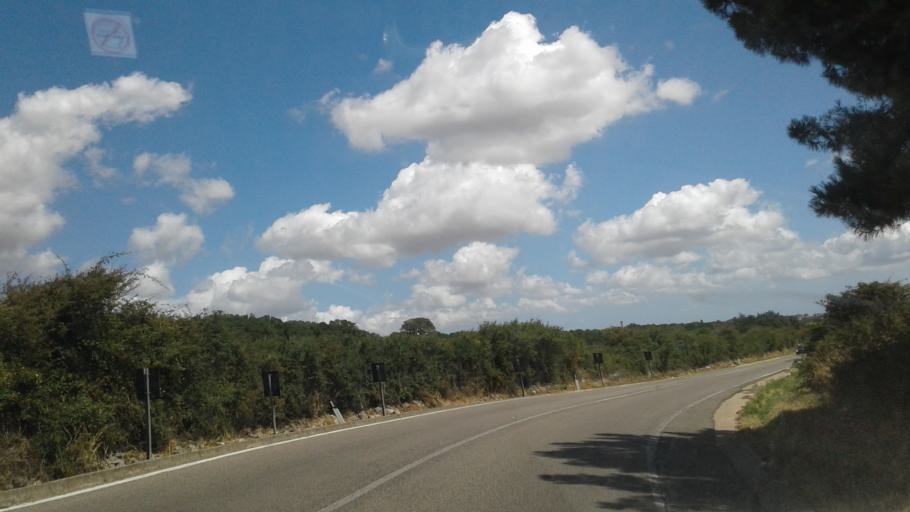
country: IT
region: Sardinia
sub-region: Provincia di Olbia-Tempio
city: Luras
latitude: 40.9077
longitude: 9.1538
